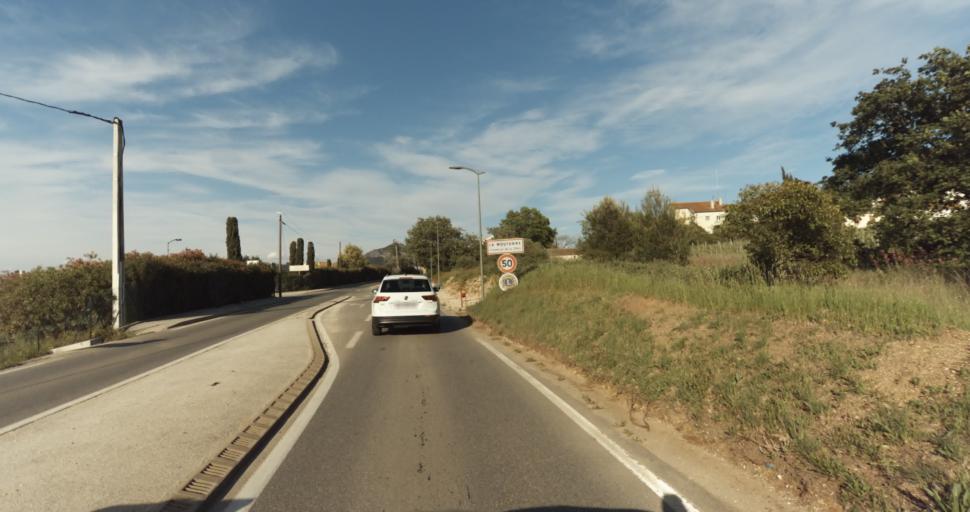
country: FR
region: Provence-Alpes-Cote d'Azur
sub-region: Departement du Var
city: Carqueiranne
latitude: 43.1184
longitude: 6.0631
